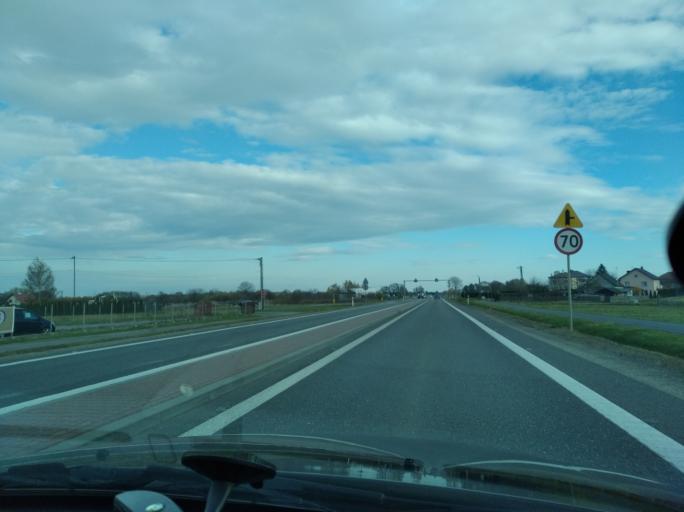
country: PL
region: Subcarpathian Voivodeship
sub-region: Powiat debicki
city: Debica
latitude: 50.0449
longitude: 21.4369
